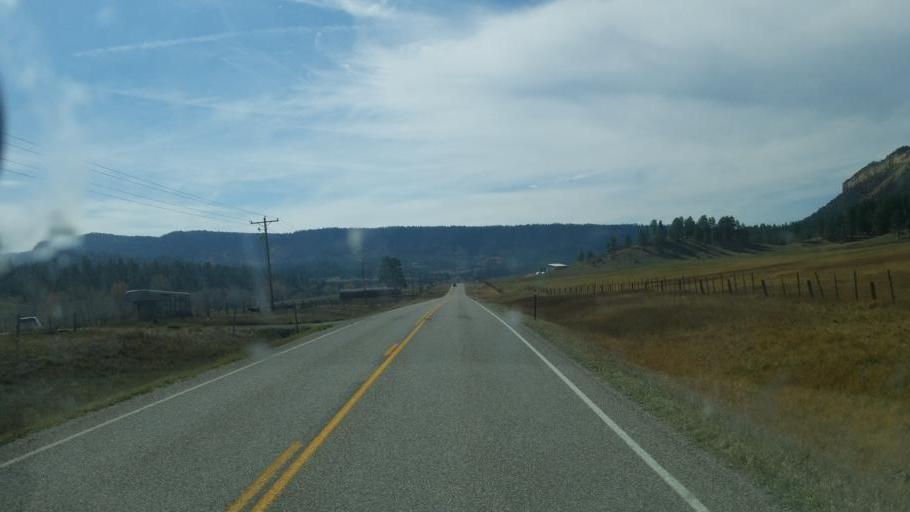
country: US
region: New Mexico
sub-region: Rio Arriba County
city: Dulce
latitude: 37.0517
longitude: -106.8403
